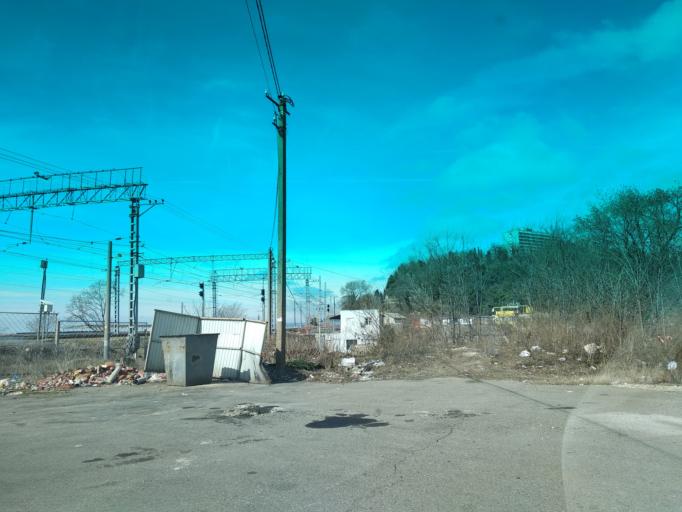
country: RU
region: Krasnodarskiy
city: Shepsi
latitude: 44.0320
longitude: 39.1441
